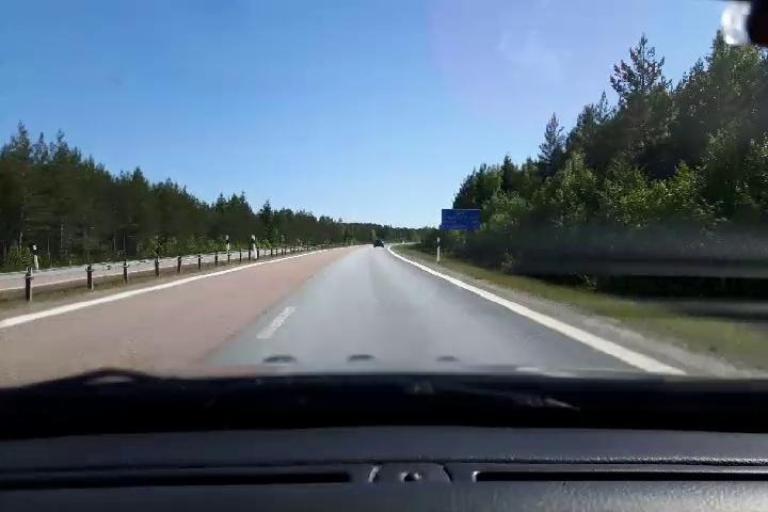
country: SE
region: Gaevleborg
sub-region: Soderhamns Kommun
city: Soderhamn
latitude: 61.4112
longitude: 16.9923
